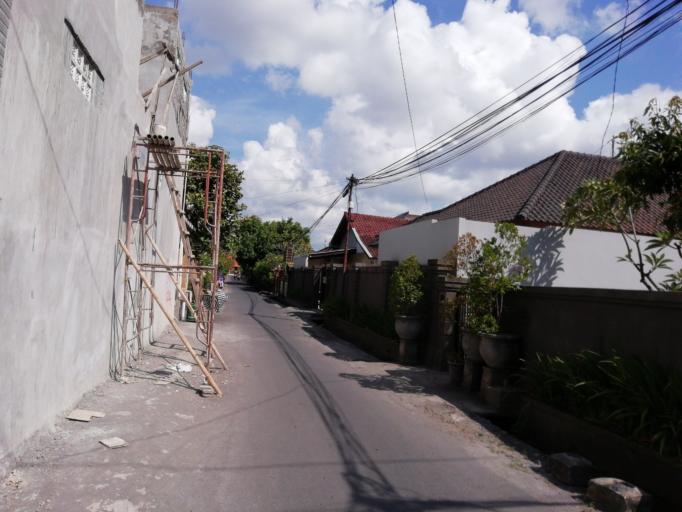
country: ID
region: Bali
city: Denpasar
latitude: -8.6721
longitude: 115.2124
